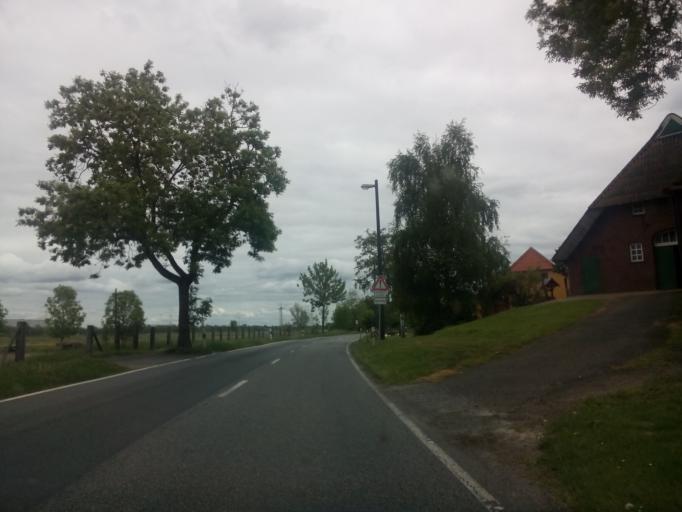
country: DE
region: Lower Saxony
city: Delmenhorst
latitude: 53.0867
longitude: 8.6888
